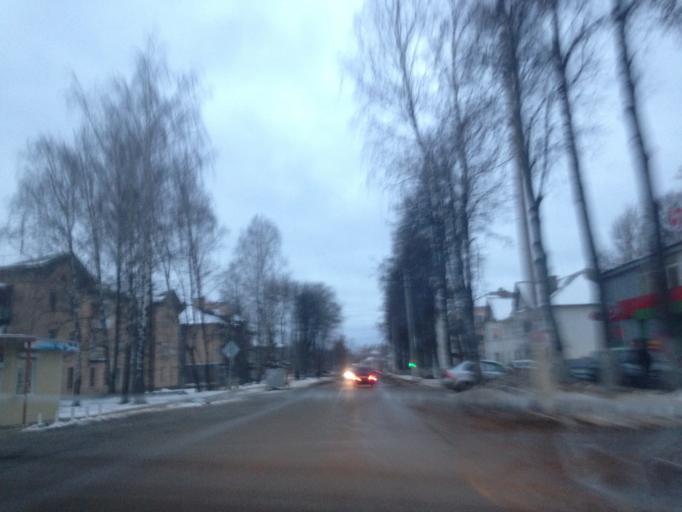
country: RU
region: Tula
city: Shchekino
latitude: 53.9984
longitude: 37.5205
